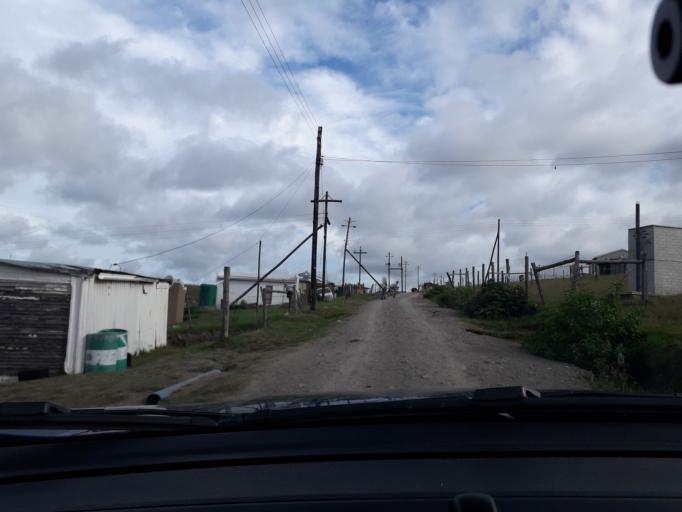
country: ZA
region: Eastern Cape
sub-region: Buffalo City Metropolitan Municipality
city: East London
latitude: -32.8511
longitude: 27.9876
